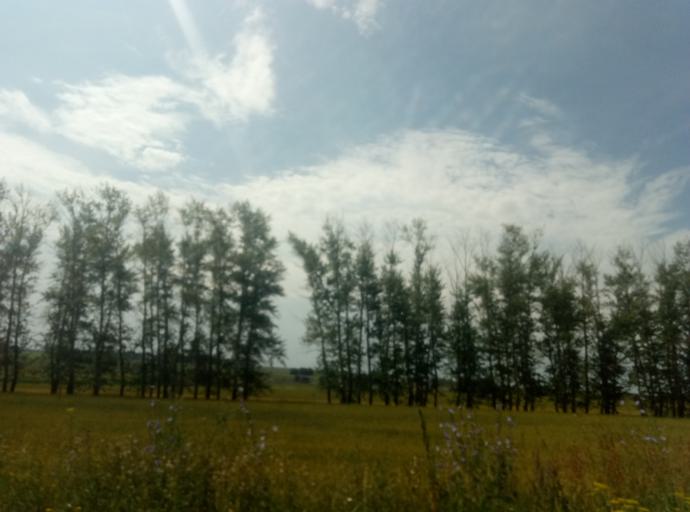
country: RU
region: Tula
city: Kireyevsk
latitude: 53.8978
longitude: 37.9883
